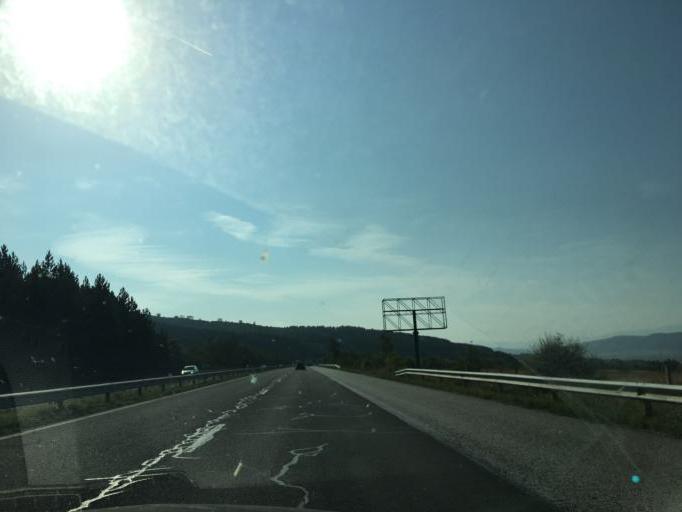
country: BG
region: Sofiya
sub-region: Obshtina Ikhtiman
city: Ikhtiman
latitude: 42.4516
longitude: 23.8421
